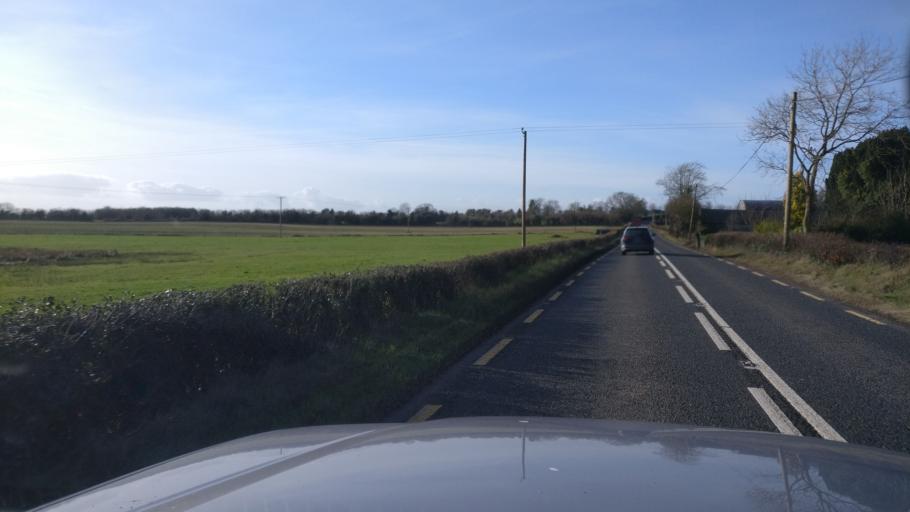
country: IE
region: Leinster
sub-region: Uibh Fhaili
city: Tullamore
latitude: 53.1981
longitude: -7.4229
